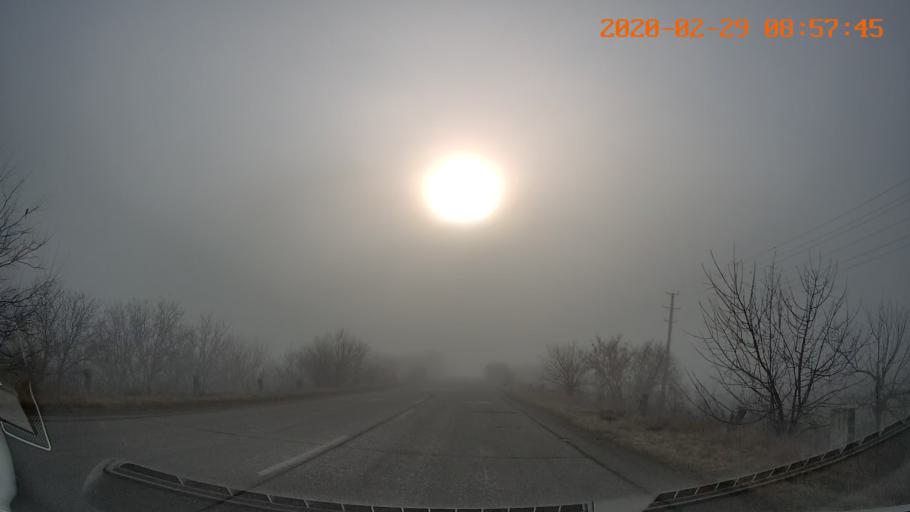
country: MD
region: Telenesti
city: Tiraspolul Nou
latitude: 46.9260
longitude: 29.6309
